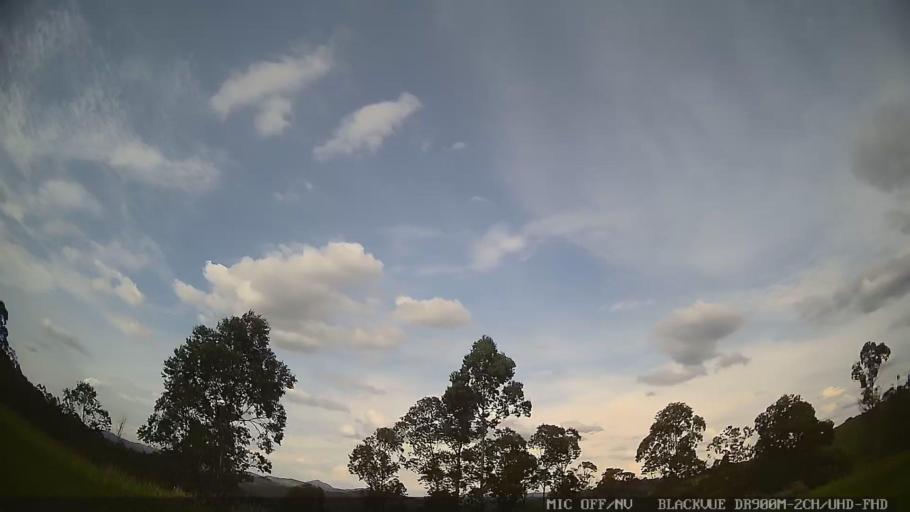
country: BR
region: Sao Paulo
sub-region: Amparo
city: Amparo
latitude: -22.7556
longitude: -46.7601
